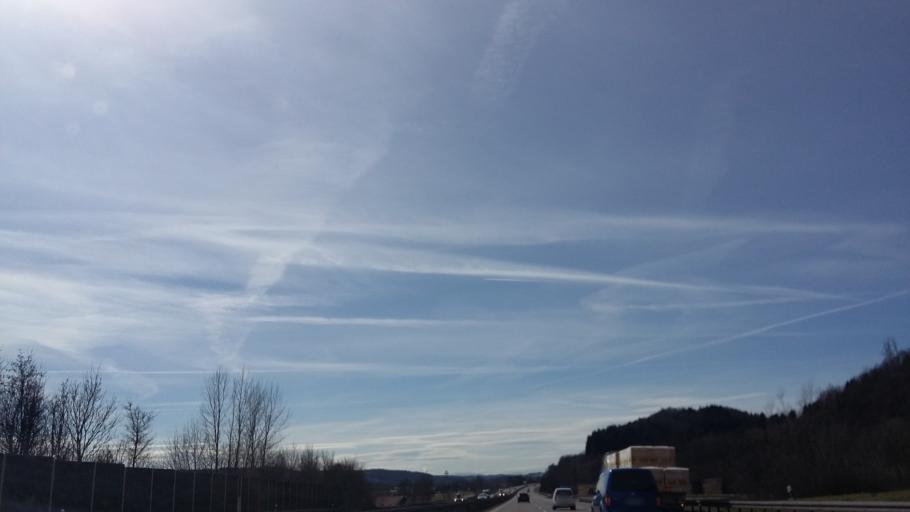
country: DE
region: Baden-Wuerttemberg
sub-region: Tuebingen Region
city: Aichstetten
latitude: 47.8875
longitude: 10.0422
